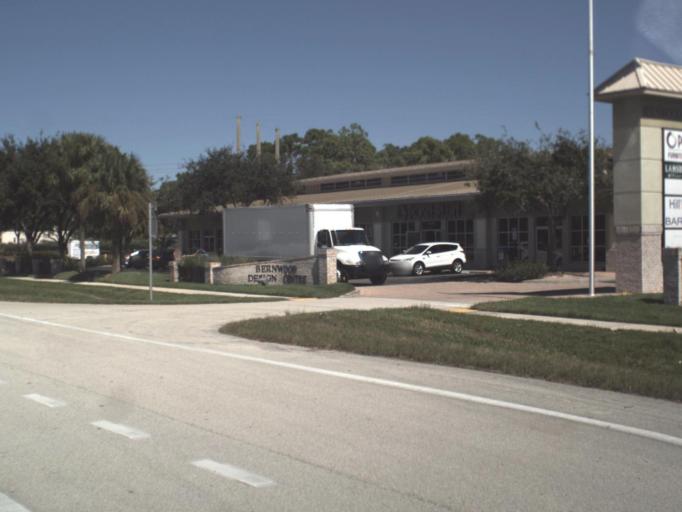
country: US
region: Florida
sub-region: Lee County
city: Bonita Springs
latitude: 26.3790
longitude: -81.8078
